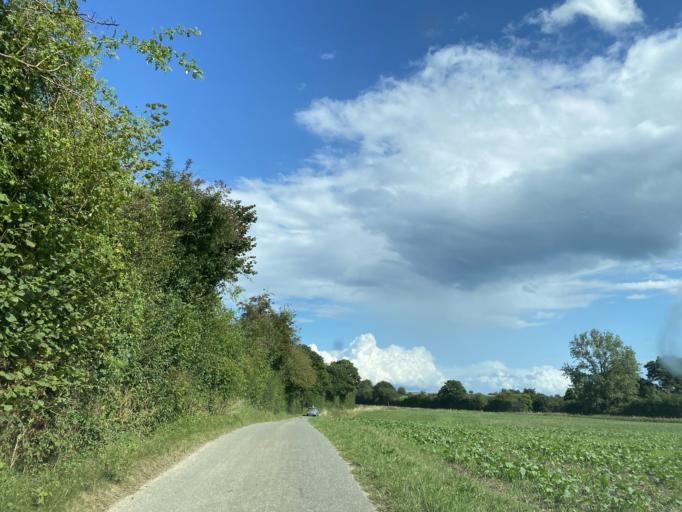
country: DK
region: South Denmark
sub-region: Haderslev Kommune
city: Starup
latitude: 55.1812
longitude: 9.5077
